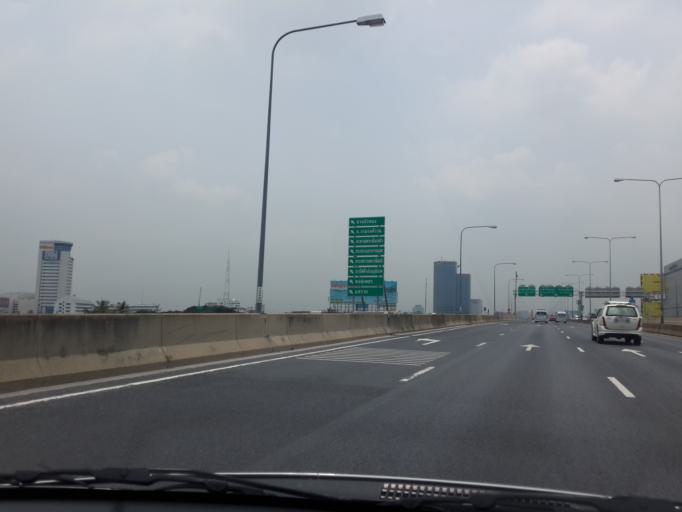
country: TH
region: Bangkok
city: Chatuchak
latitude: 13.8437
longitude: 100.5593
